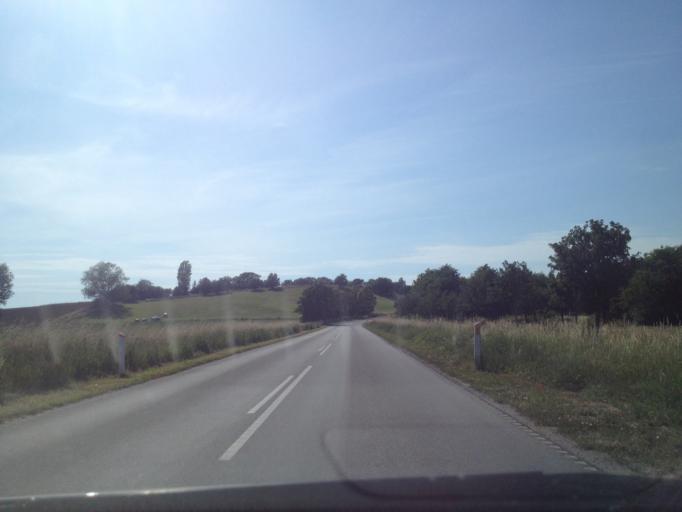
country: DK
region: Central Jutland
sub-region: Samso Kommune
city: Tranebjerg
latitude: 55.8595
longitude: 10.5685
